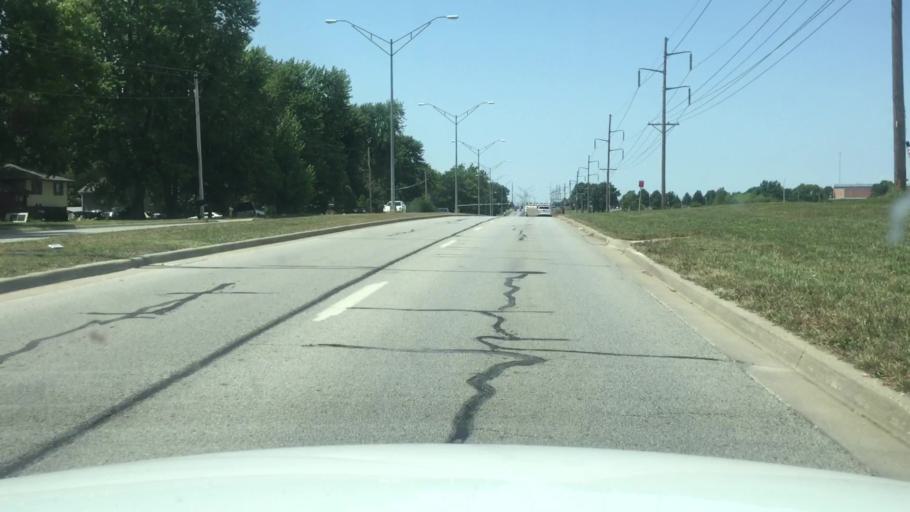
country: US
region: Missouri
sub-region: Jackson County
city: Lees Summit
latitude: 38.9255
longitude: -94.3907
